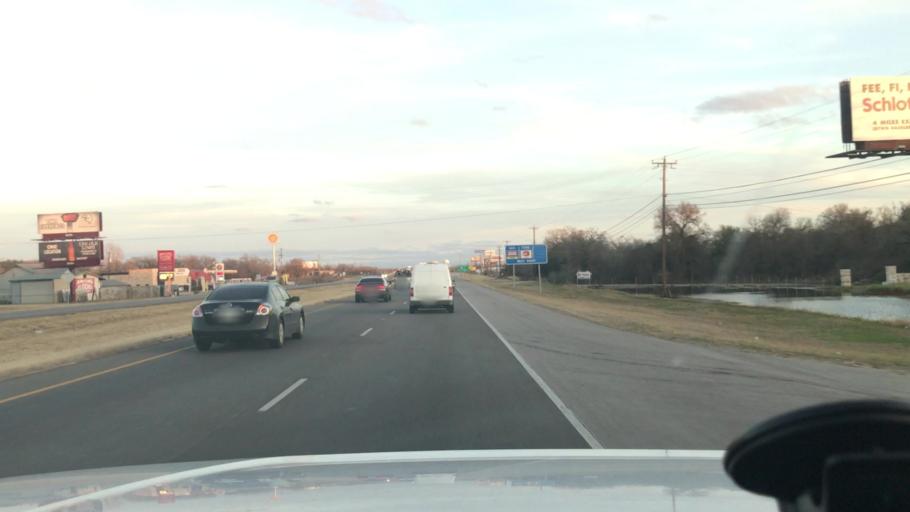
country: US
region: Texas
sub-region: Bastrop County
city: Wyldwood
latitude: 30.1172
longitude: -97.4241
